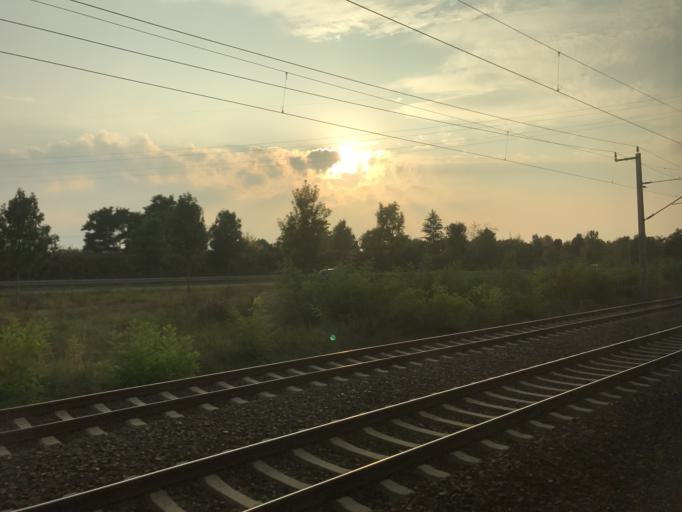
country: DE
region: Saxony
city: Leipzig
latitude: 51.3832
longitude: 12.3129
